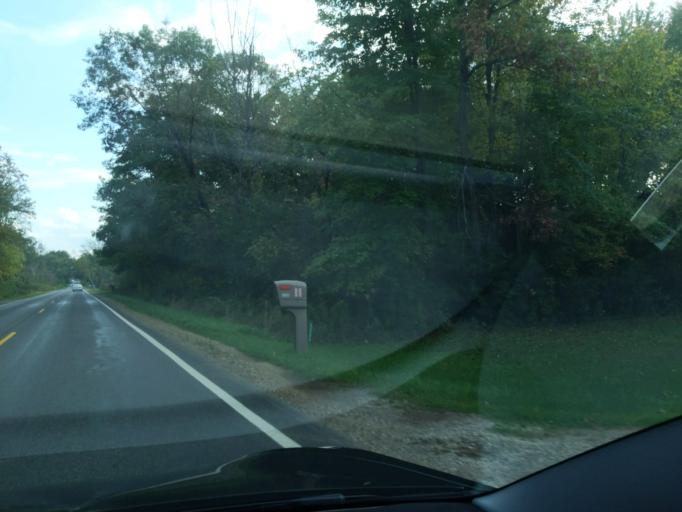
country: US
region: Michigan
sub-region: Jackson County
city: Jackson
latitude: 42.2994
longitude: -84.4626
